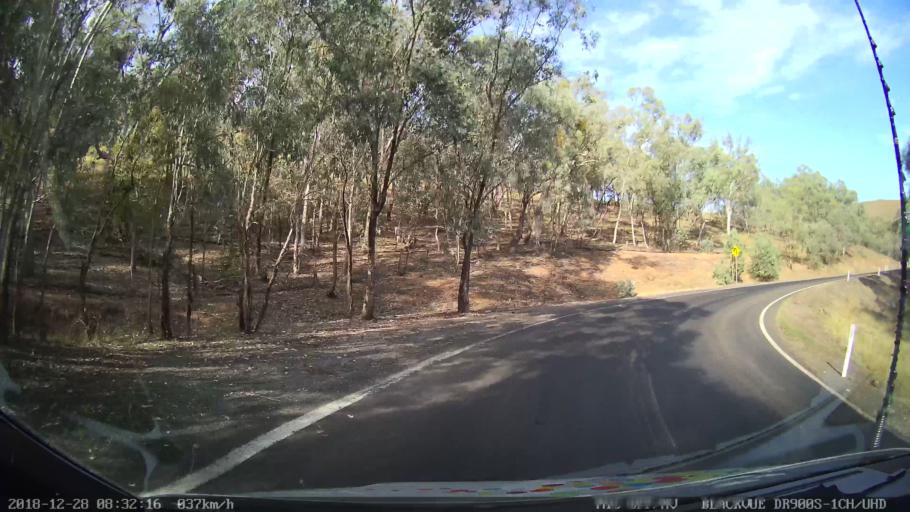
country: AU
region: New South Wales
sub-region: Blayney
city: Blayney
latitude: -33.9637
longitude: 149.3146
